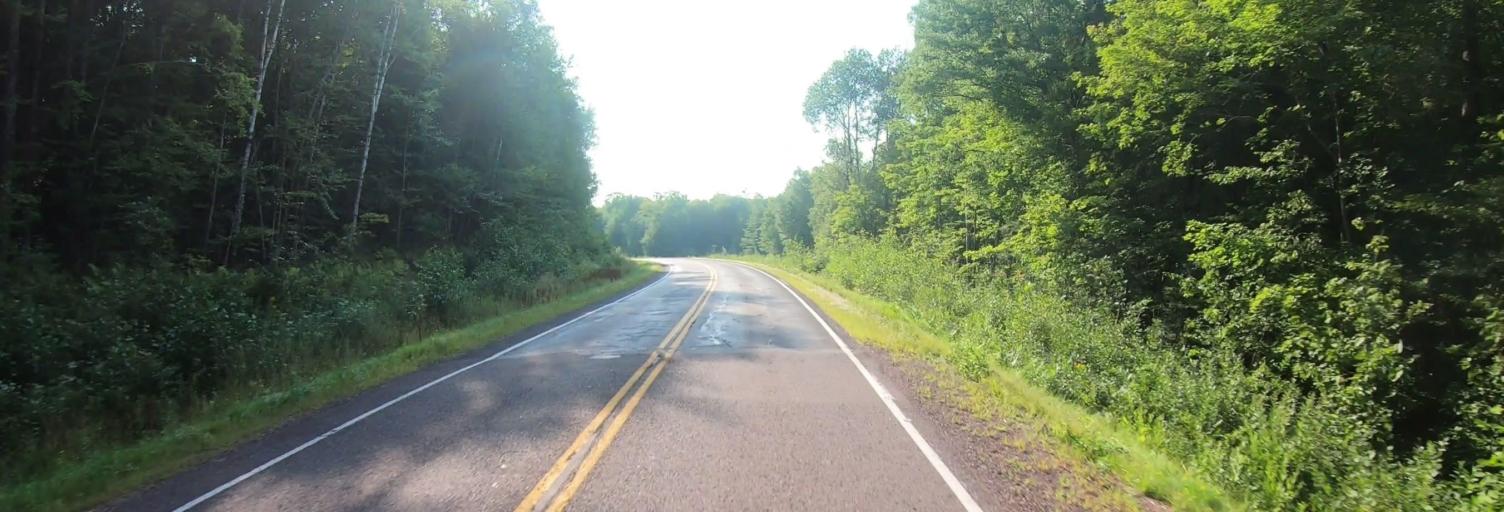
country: US
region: Wisconsin
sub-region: Ashland County
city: Ashland
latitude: 46.2943
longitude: -90.8107
